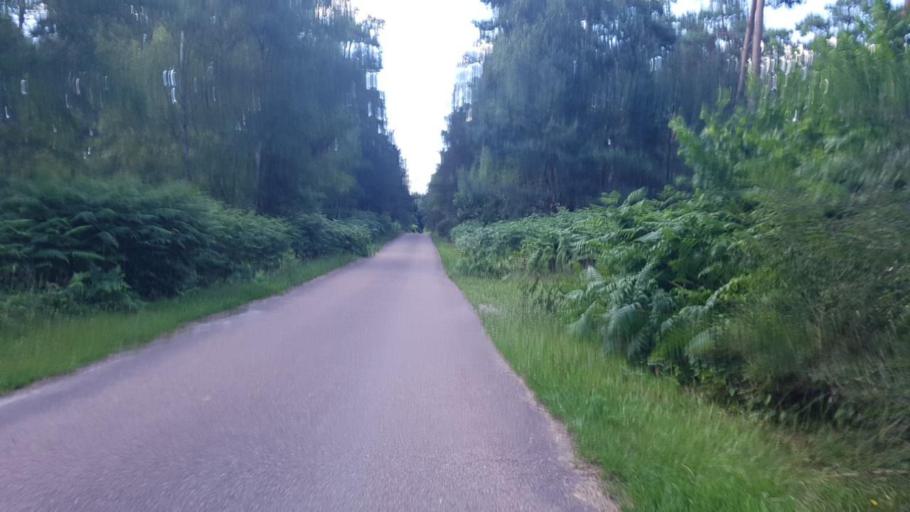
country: FR
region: Picardie
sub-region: Departement de l'Oise
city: Ver-sur-Launette
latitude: 49.1530
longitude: 2.6387
